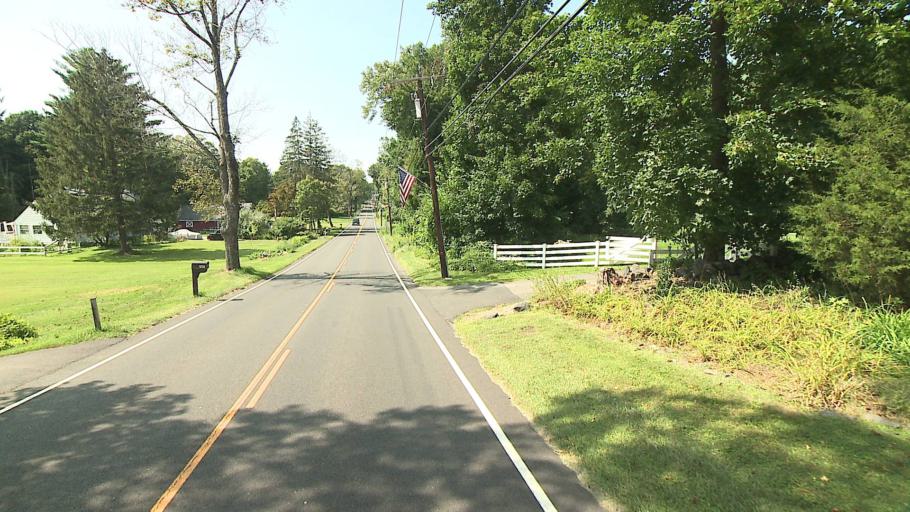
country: US
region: Connecticut
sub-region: Fairfield County
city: Danbury
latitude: 41.4730
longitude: -73.3939
